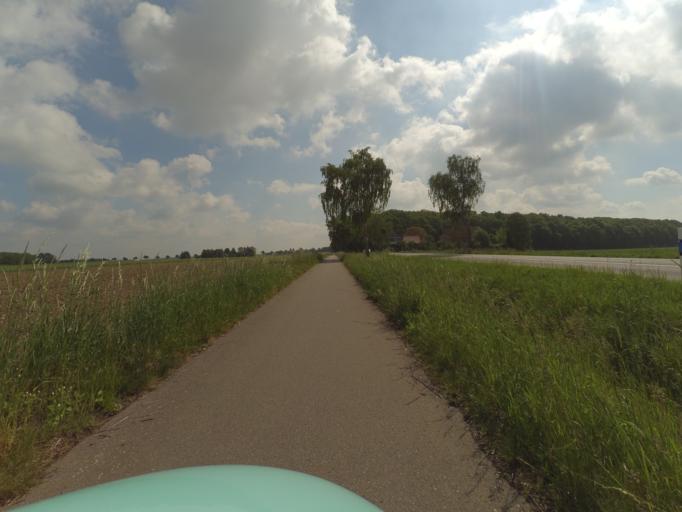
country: DE
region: Lower Saxony
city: Edemissen
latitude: 52.3876
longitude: 10.2394
